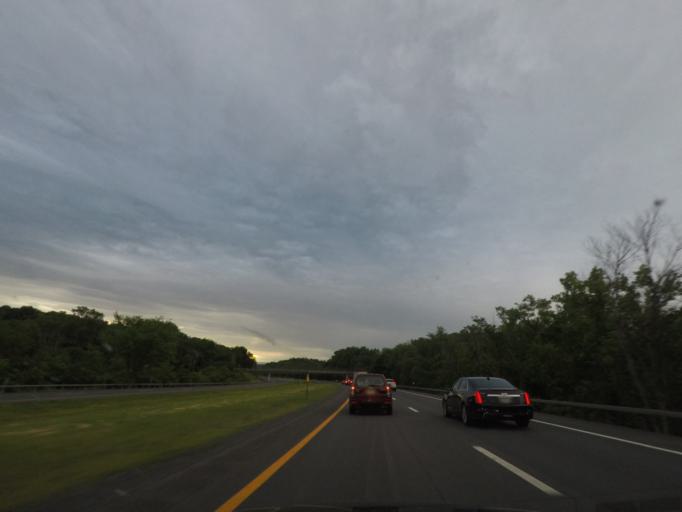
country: US
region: New York
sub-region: Columbia County
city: Chatham
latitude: 42.4433
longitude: -73.5578
